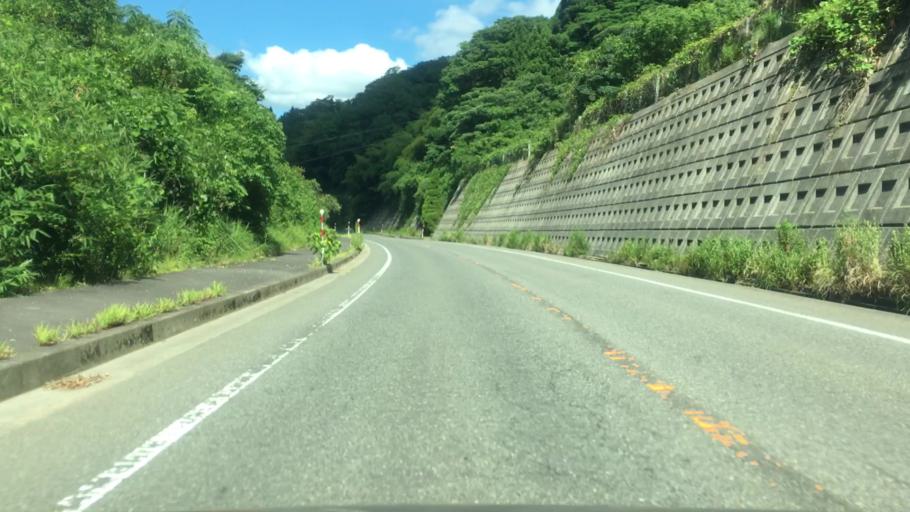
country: JP
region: Hyogo
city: Toyooka
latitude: 35.5758
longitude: 134.7625
